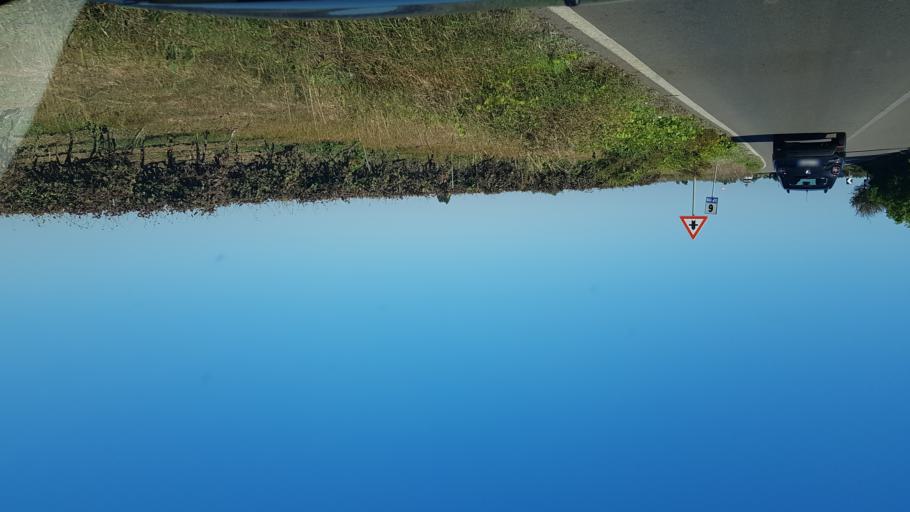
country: IT
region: Apulia
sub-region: Provincia di Lecce
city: Carmiano
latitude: 40.3137
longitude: 18.0412
